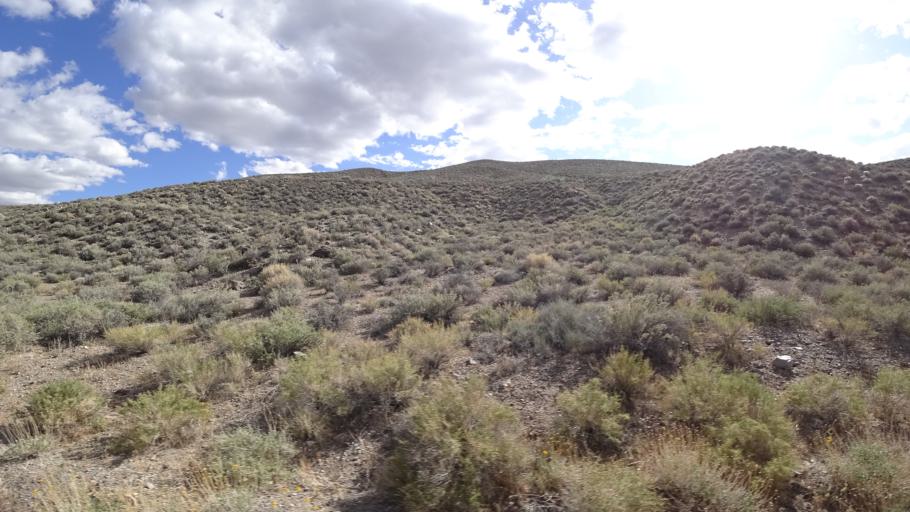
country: US
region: Nevada
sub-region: Nye County
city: Beatty
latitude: 36.4035
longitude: -117.1698
